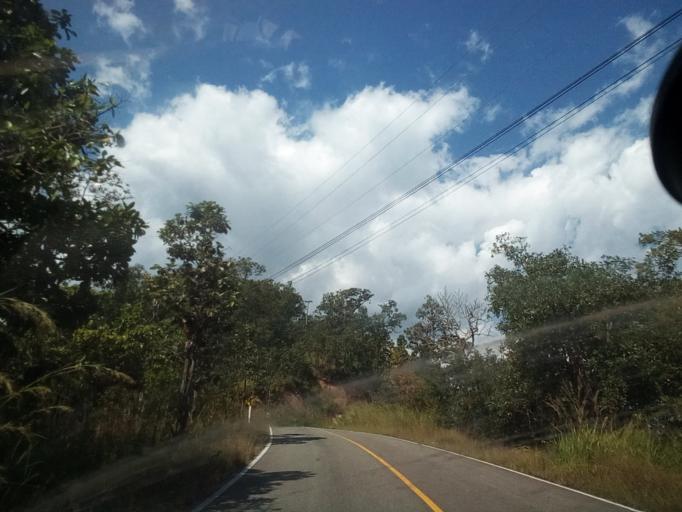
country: TH
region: Chiang Mai
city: Samoeng
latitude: 18.8714
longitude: 98.6904
